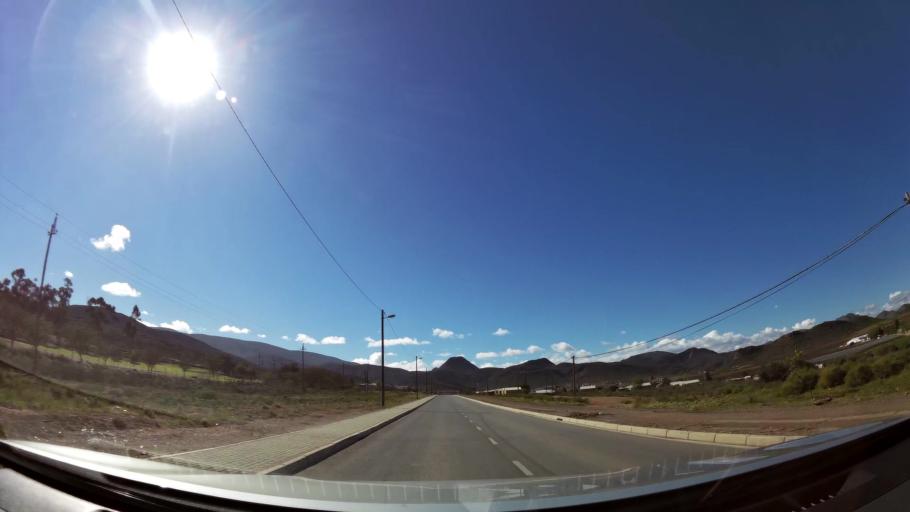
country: ZA
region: Western Cape
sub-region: Cape Winelands District Municipality
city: Ashton
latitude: -33.7716
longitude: 20.1384
